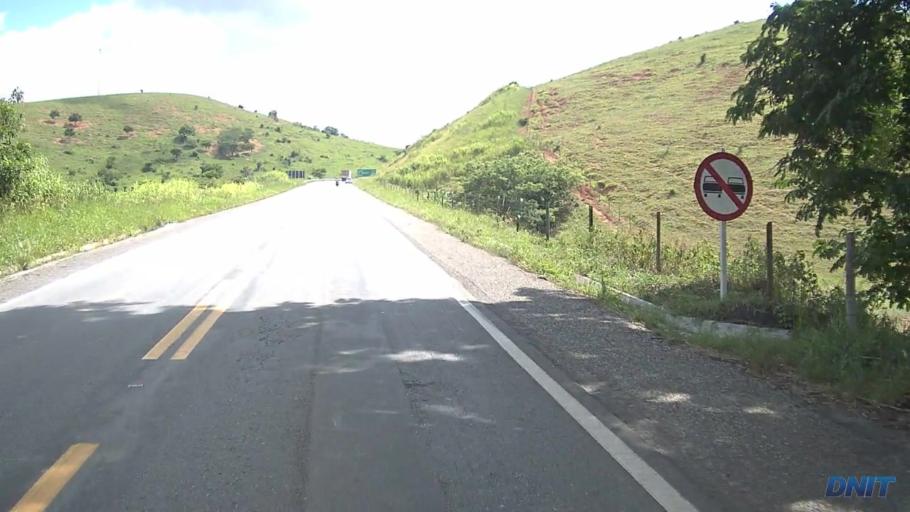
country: BR
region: Minas Gerais
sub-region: Governador Valadares
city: Governador Valadares
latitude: -19.0264
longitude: -42.1469
